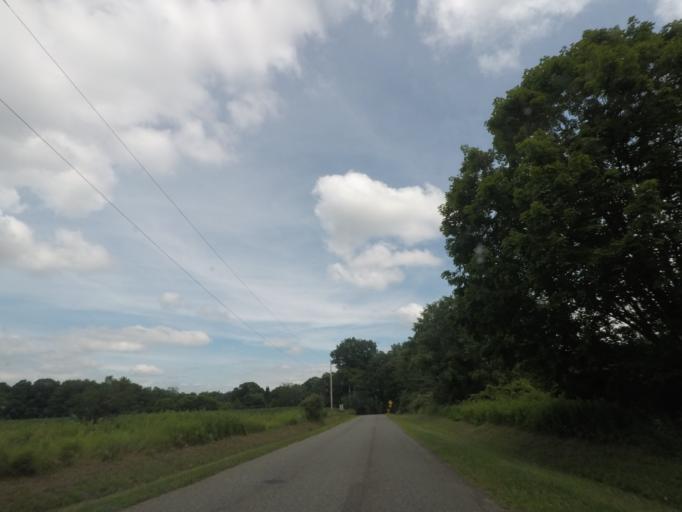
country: US
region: New York
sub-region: Saratoga County
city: Stillwater
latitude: 43.0095
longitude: -73.6266
